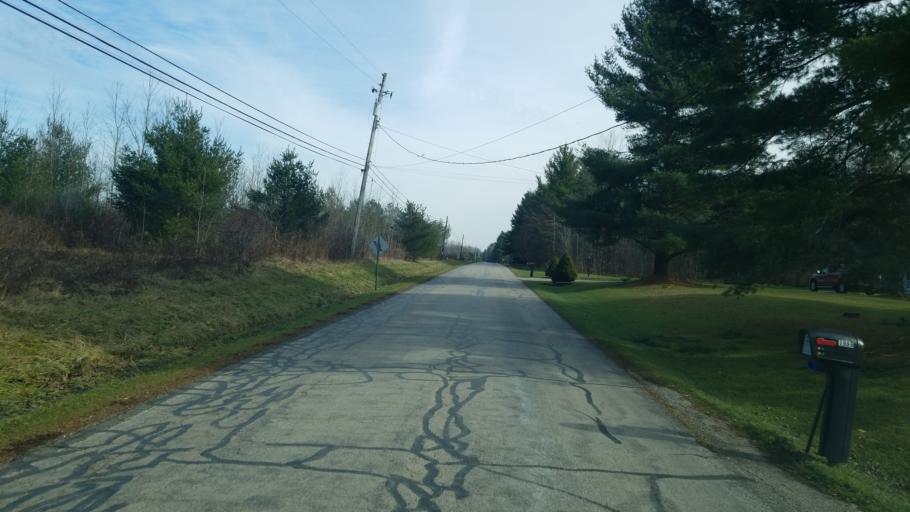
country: US
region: Ohio
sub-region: Ashtabula County
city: Roaming Shores
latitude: 41.6546
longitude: -80.8233
